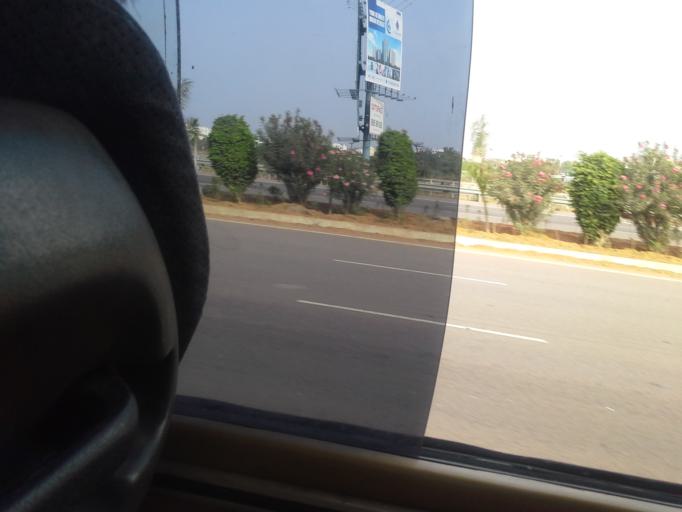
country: IN
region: Telangana
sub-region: Hyderabad
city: Hyderabad
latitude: 17.3913
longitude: 78.3517
